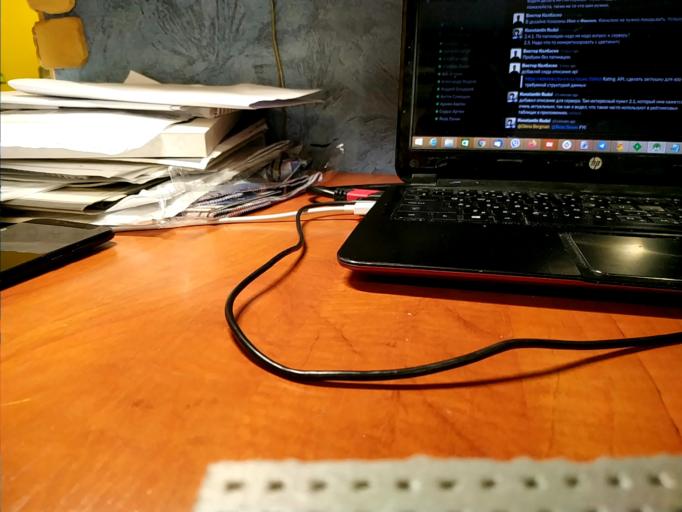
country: RU
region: Tverskaya
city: Spirovo
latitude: 57.4513
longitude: 34.9189
